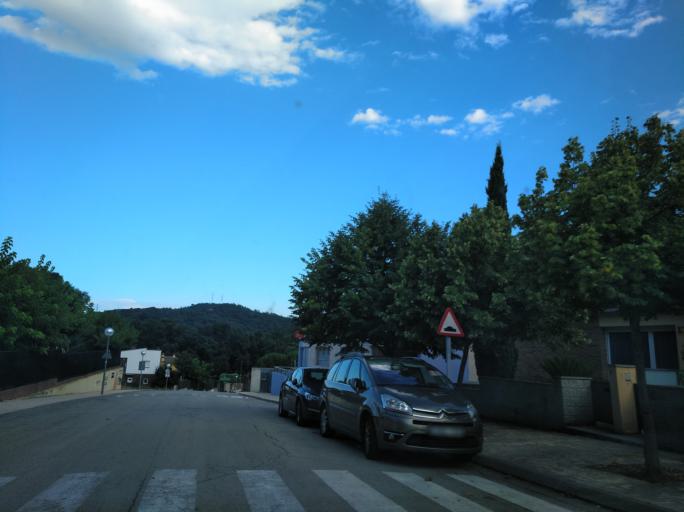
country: ES
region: Catalonia
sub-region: Provincia de Girona
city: Angles
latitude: 41.9701
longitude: 2.6645
